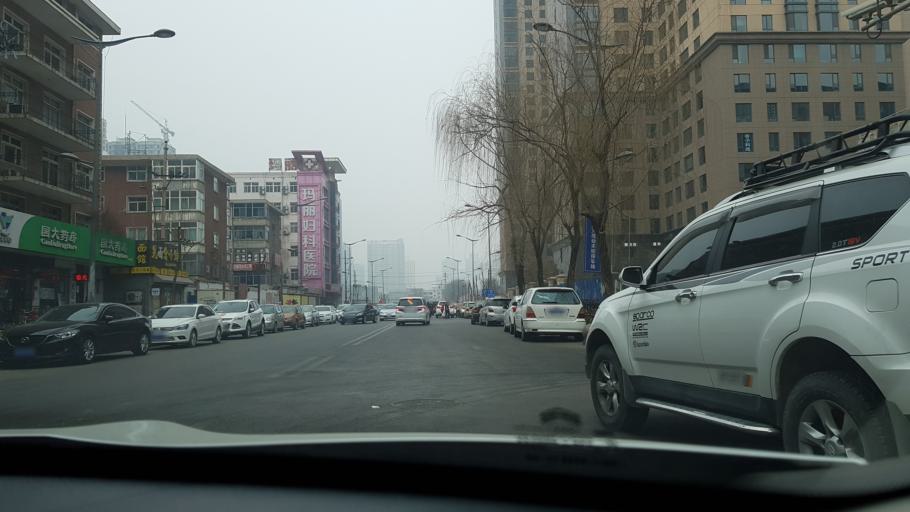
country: CN
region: Shanxi Sheng
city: Taiyuan
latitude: 37.8239
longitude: 112.5586
